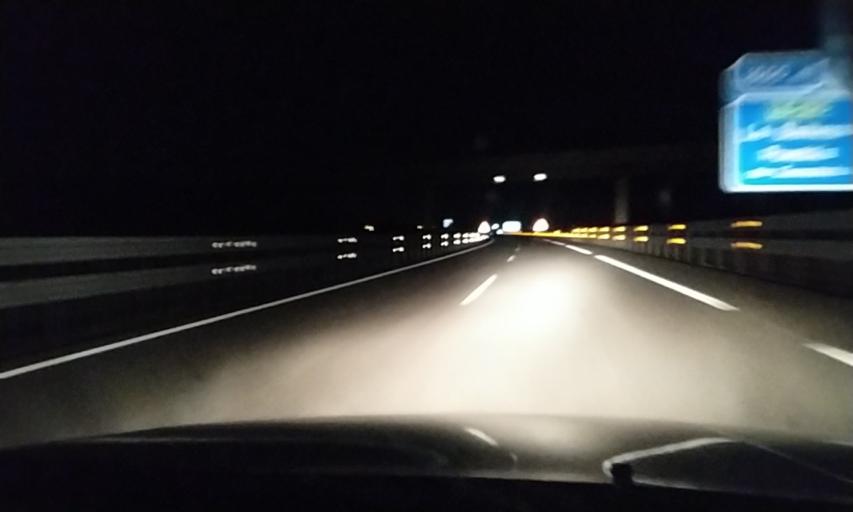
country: ES
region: Castille and Leon
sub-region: Provincia de Leon
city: La Baneza
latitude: 42.2977
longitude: -5.9281
